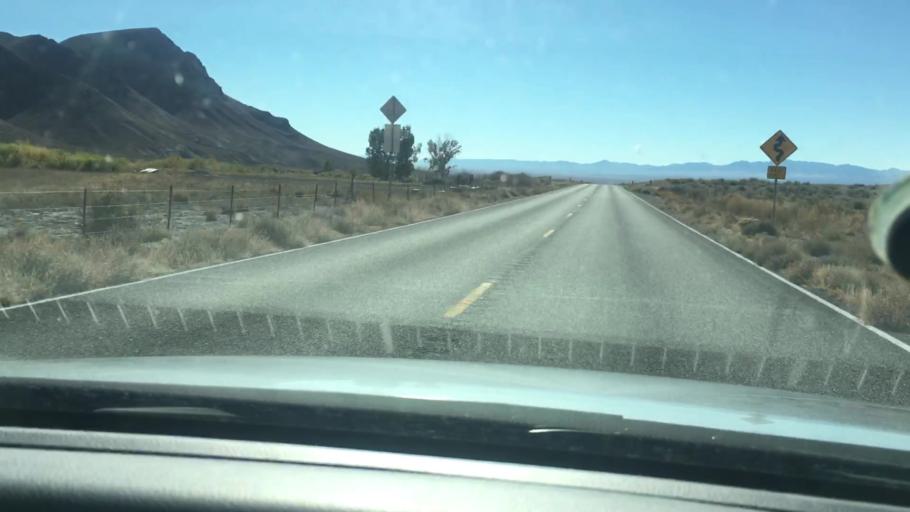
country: US
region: Nevada
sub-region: White Pine County
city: Ely
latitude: 38.7603
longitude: -115.4419
